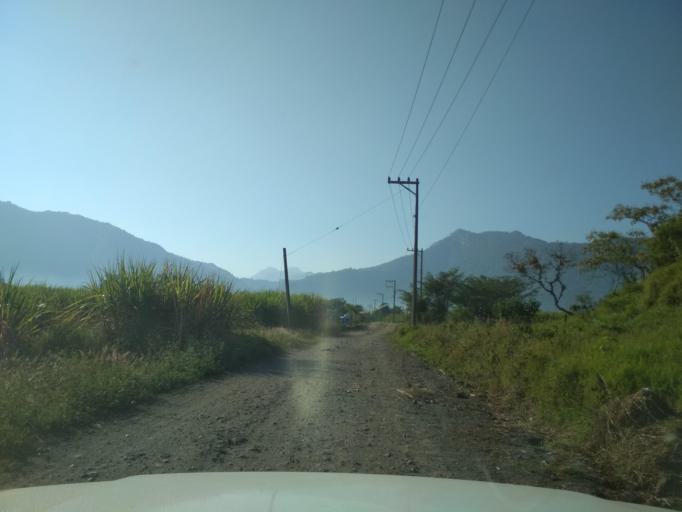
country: MX
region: Veracruz
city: Jalapilla
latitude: 18.8289
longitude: -97.0803
